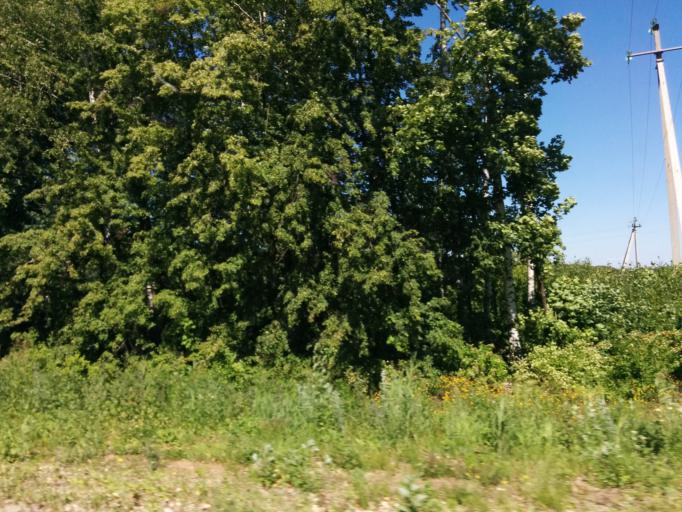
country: RU
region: Tambov
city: Morshansk
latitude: 53.5804
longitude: 41.7428
